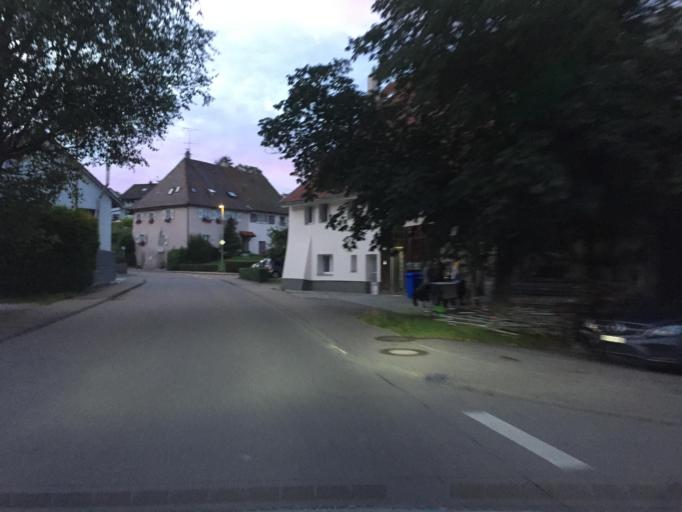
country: DE
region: Baden-Wuerttemberg
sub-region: Freiburg Region
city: Eggingen
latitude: 47.6613
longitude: 8.4204
